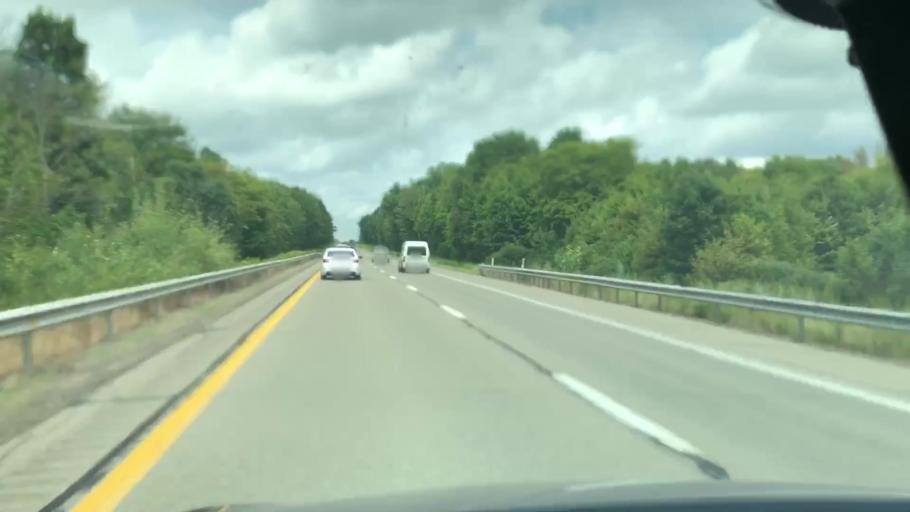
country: US
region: Pennsylvania
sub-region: Crawford County
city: Meadville
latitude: 41.7501
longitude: -80.1969
